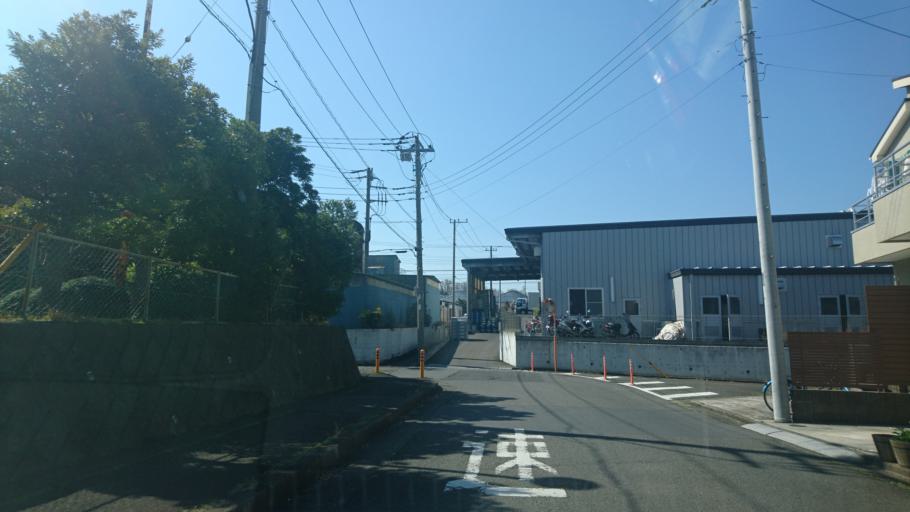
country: JP
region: Kanagawa
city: Fujisawa
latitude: 35.4007
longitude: 139.4273
